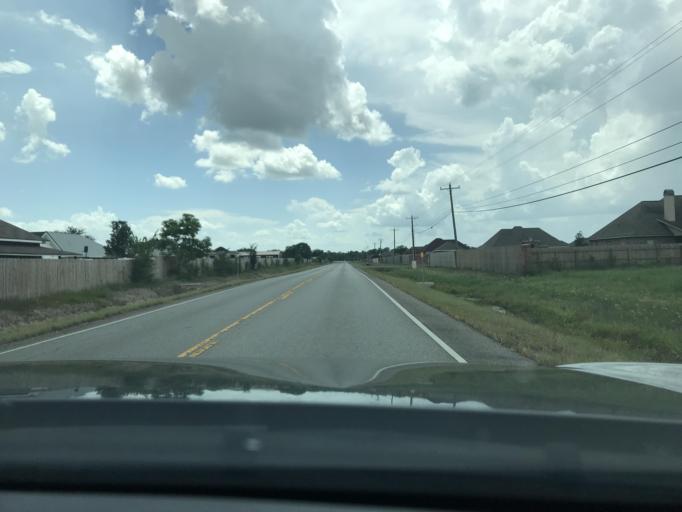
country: US
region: Louisiana
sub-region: Calcasieu Parish
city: Moss Bluff
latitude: 30.3407
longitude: -93.2343
